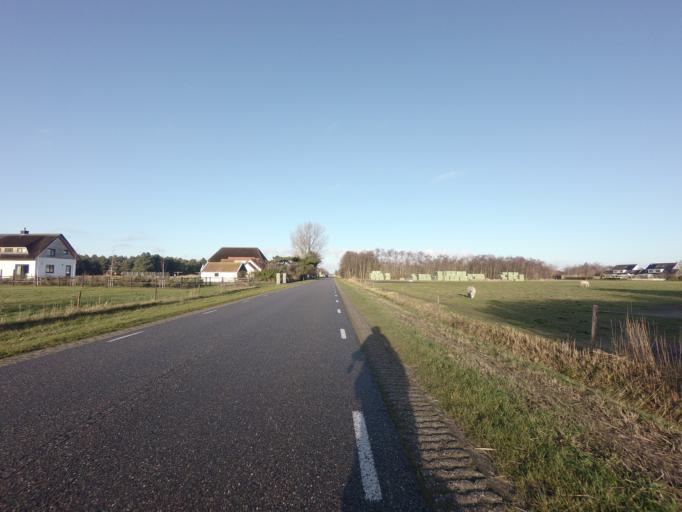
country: NL
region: North Holland
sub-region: Gemeente Texel
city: Den Burg
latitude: 53.1534
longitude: 4.8650
